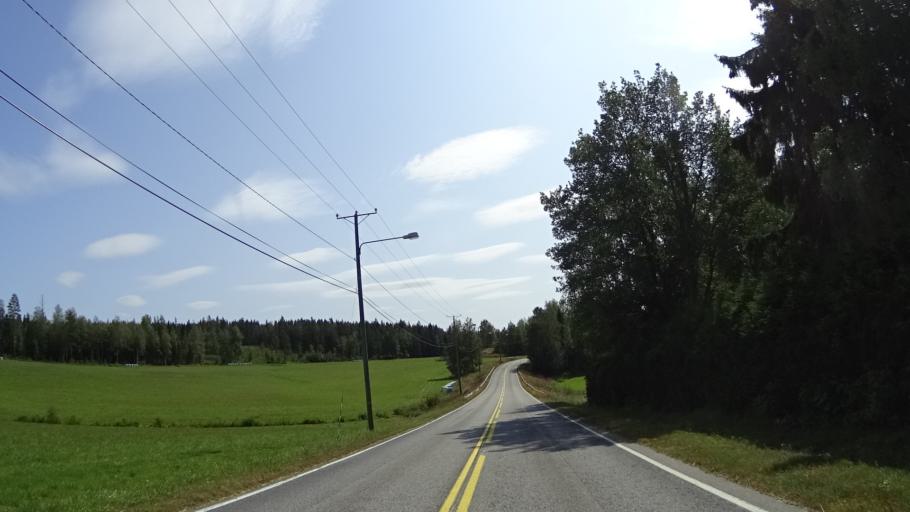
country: FI
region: Pirkanmaa
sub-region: Ylae-Pirkanmaa
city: Maenttae
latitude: 61.9096
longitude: 24.7834
